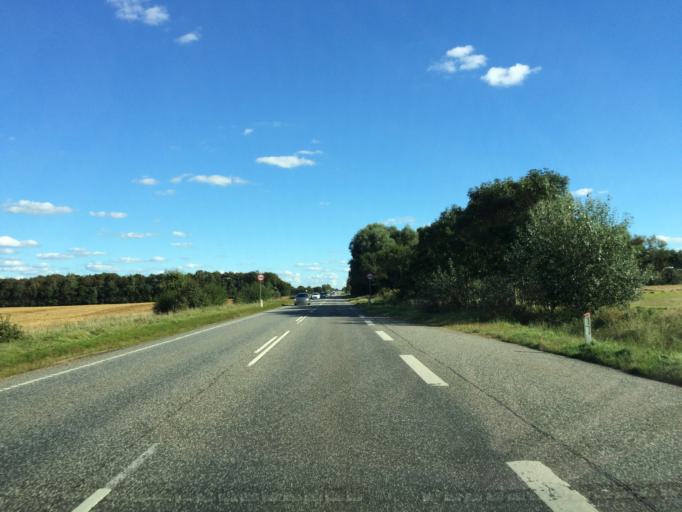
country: DK
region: Central Jutland
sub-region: Holstebro Kommune
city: Holstebro
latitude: 56.3242
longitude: 8.6695
